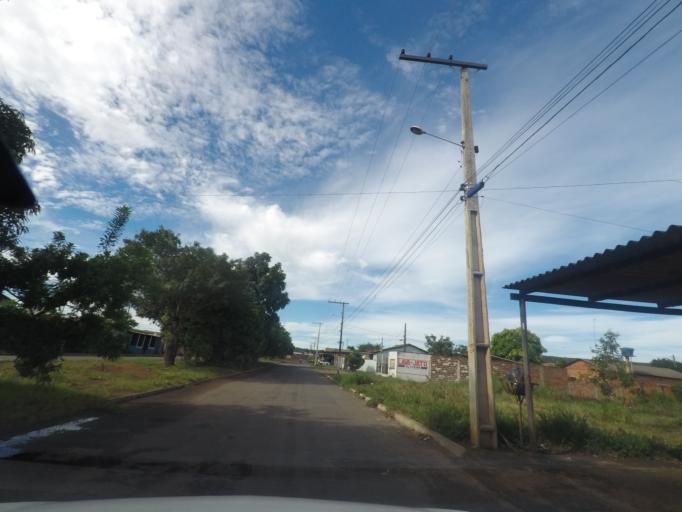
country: BR
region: Goias
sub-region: Aparecida De Goiania
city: Aparecida de Goiania
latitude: -16.8276
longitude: -49.2977
